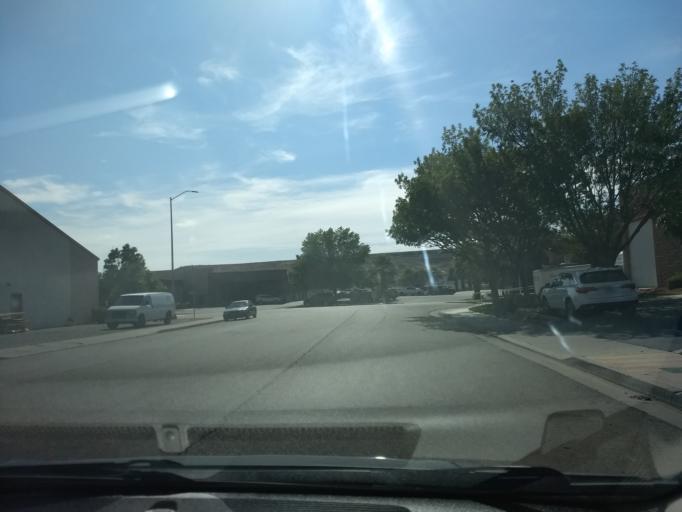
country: US
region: Utah
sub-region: Washington County
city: Saint George
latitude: 37.0845
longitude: -113.5775
